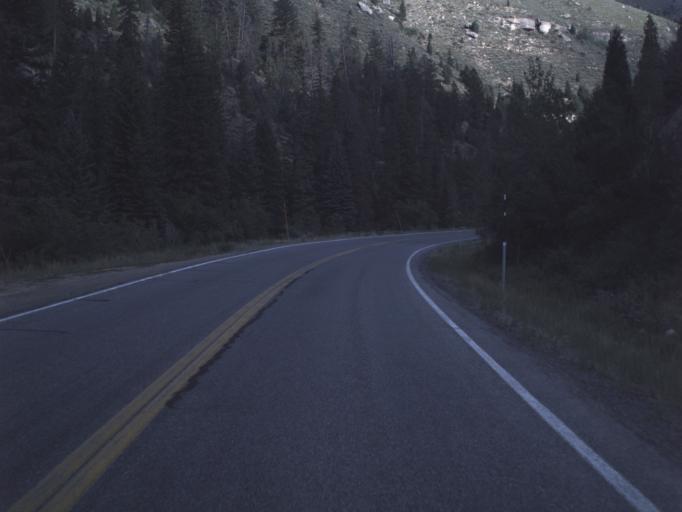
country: US
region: Utah
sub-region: Emery County
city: Huntington
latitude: 39.4759
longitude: -111.1575
